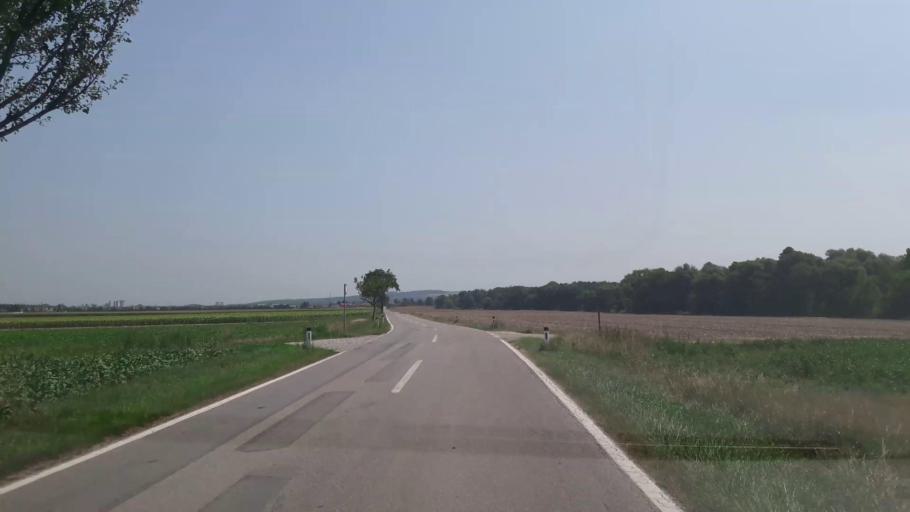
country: AT
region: Lower Austria
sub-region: Politischer Bezirk Bruck an der Leitha
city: Sommerein
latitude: 48.0174
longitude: 16.7007
